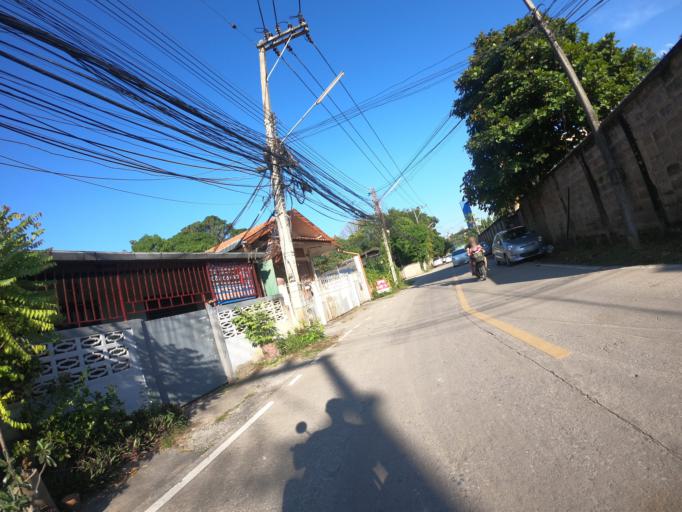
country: TH
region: Chiang Mai
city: Chiang Mai
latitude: 18.7906
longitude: 99.0075
